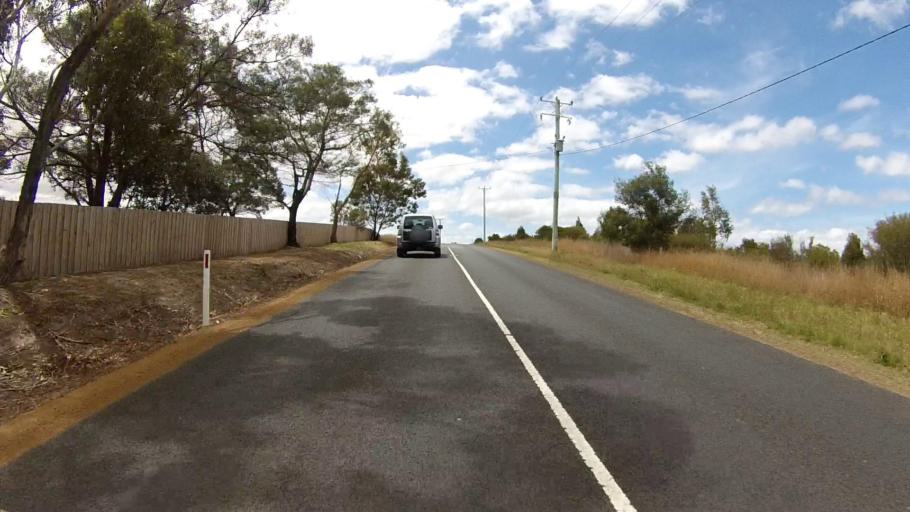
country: AU
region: Tasmania
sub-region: Sorell
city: Sorell
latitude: -42.8151
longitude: 147.6132
